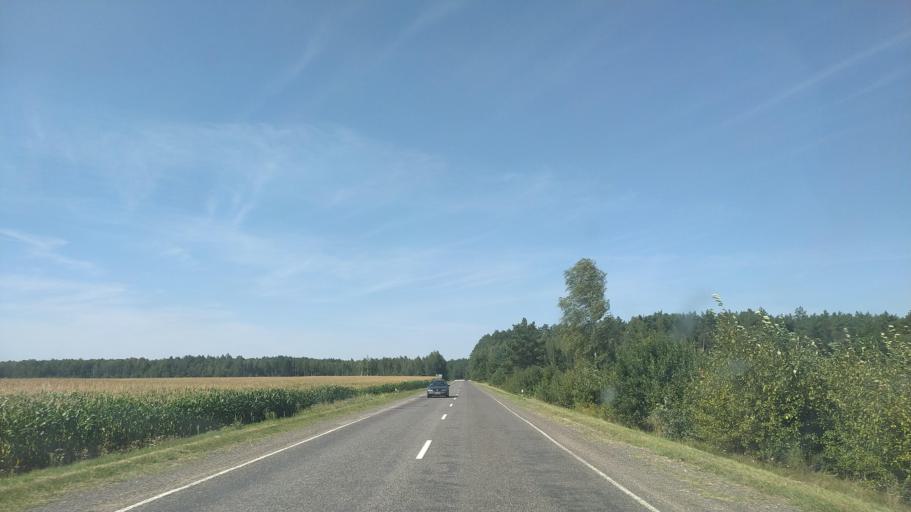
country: BY
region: Brest
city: Byaroza
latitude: 52.4009
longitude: 25.0034
